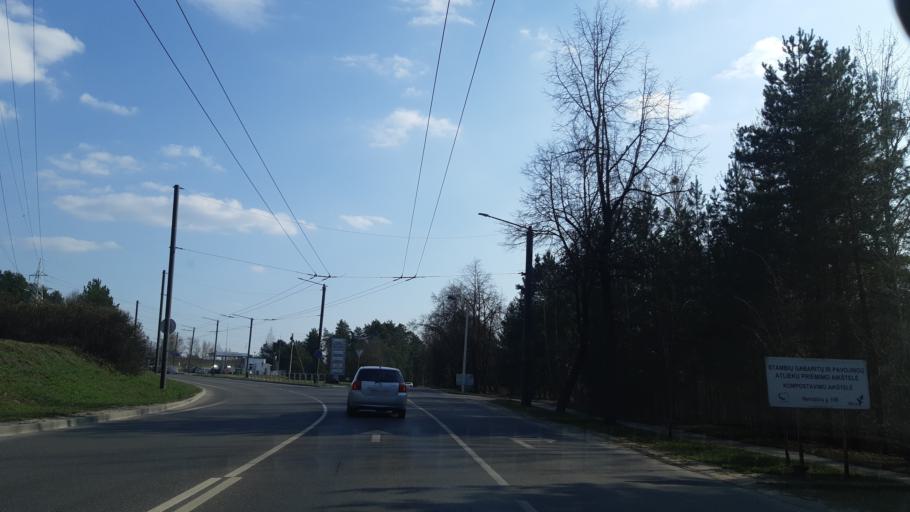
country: LT
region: Kauno apskritis
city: Dainava (Kaunas)
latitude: 54.8825
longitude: 24.0084
